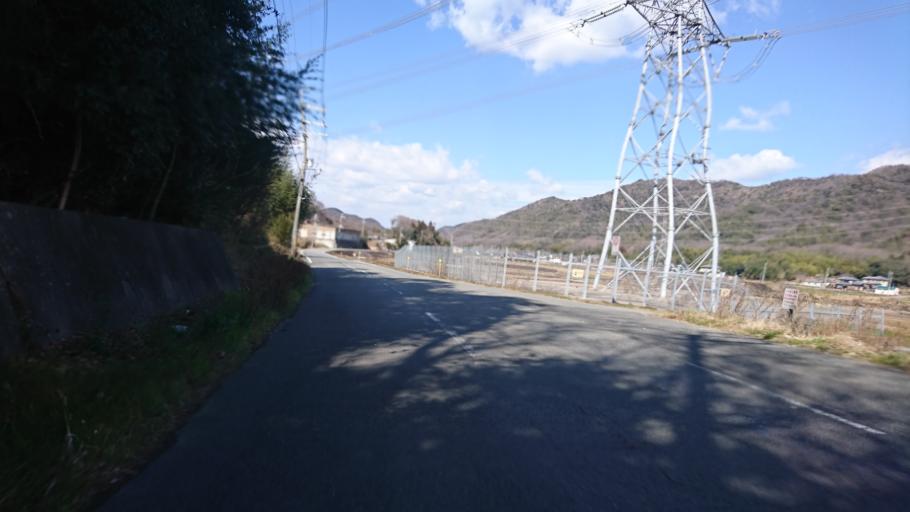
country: JP
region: Hyogo
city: Kakogawacho-honmachi
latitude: 34.8375
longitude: 134.8214
